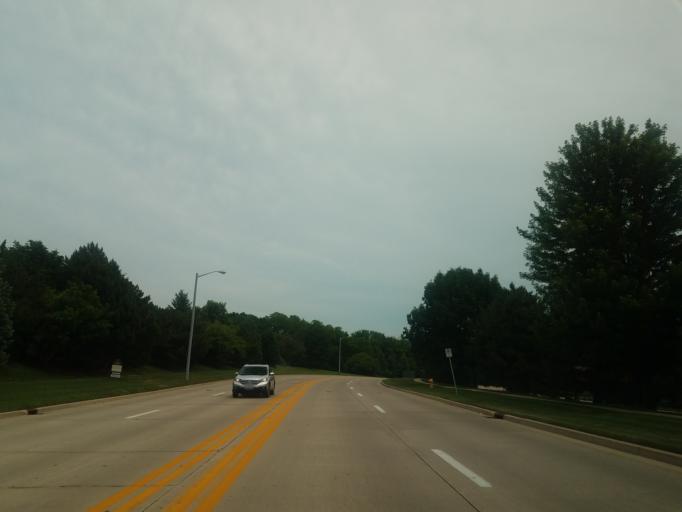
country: US
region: Illinois
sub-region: McLean County
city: Normal
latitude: 40.5052
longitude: -88.9405
